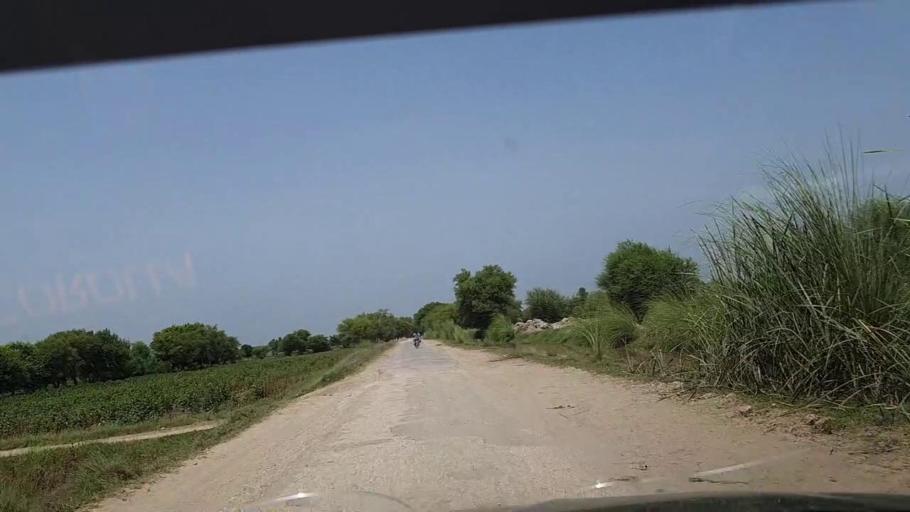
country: PK
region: Sindh
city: Khanpur
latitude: 27.8092
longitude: 69.4505
